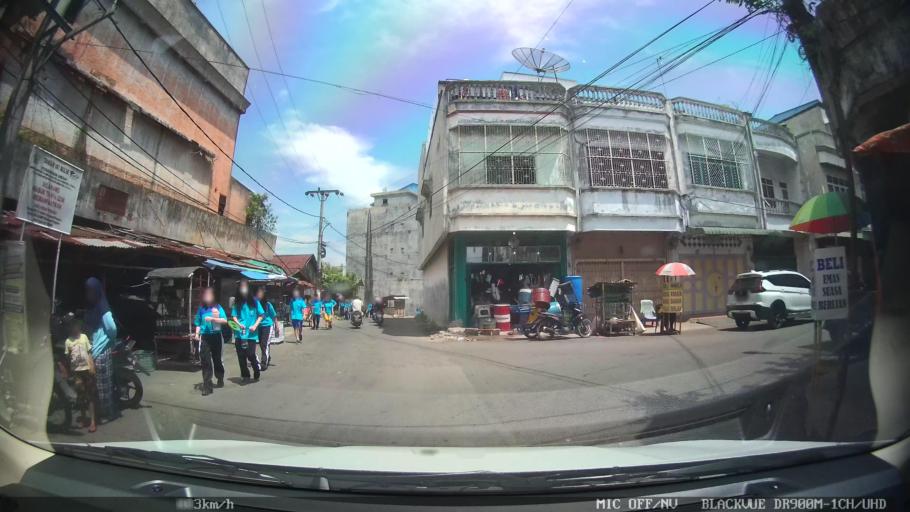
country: ID
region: North Sumatra
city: Binjai
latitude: 3.6064
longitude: 98.4876
